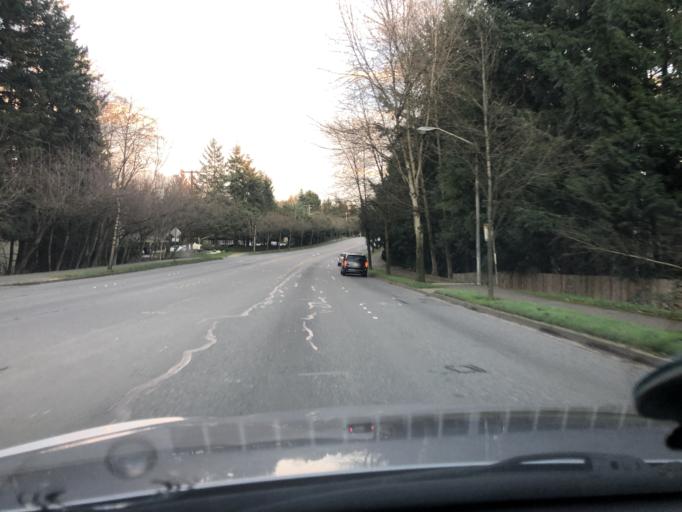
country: US
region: Washington
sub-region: King County
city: Federal Way
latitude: 47.3150
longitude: -122.3388
